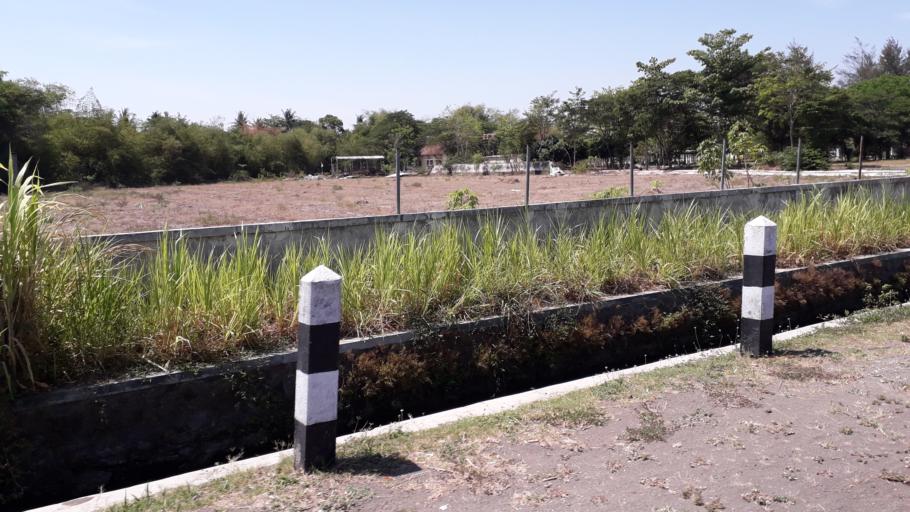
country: ID
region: Daerah Istimewa Yogyakarta
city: Pundong
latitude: -7.9437
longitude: 110.3319
